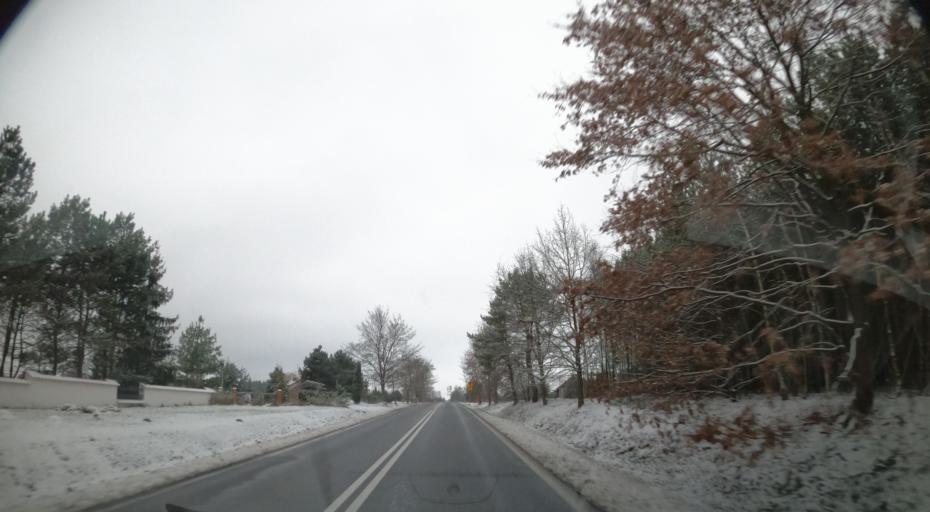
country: PL
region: Masovian Voivodeship
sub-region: Powiat plocki
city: Nowy Duninow
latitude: 52.5890
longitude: 19.5142
